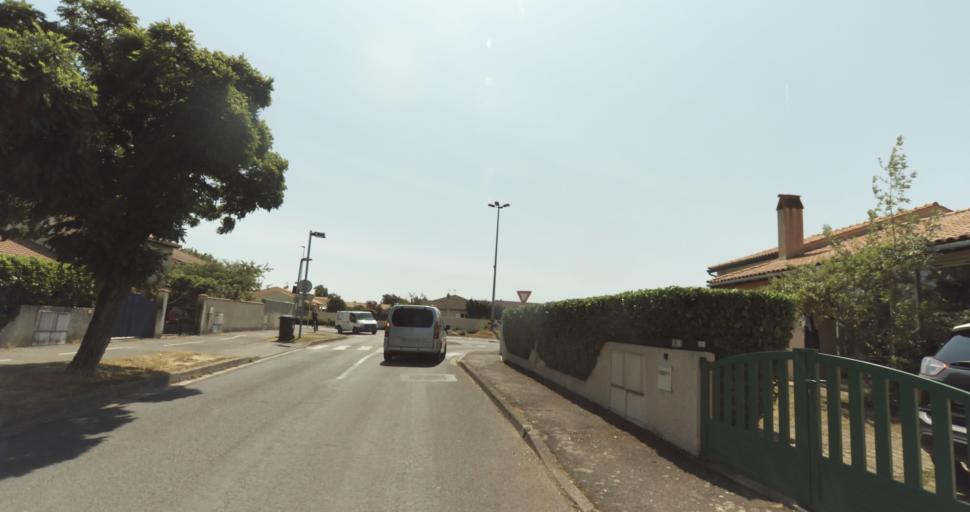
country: FR
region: Midi-Pyrenees
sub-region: Departement de la Haute-Garonne
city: Plaisance-du-Touch
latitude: 43.5623
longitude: 1.3094
